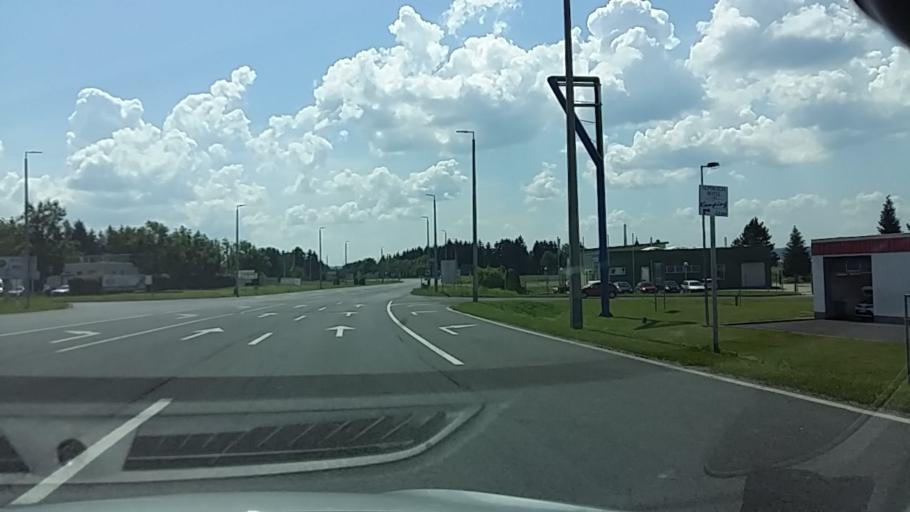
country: AT
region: Burgenland
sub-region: Politischer Bezirk Jennersdorf
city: Heiligenkreuz im Lafnitztal
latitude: 46.9824
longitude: 16.2811
